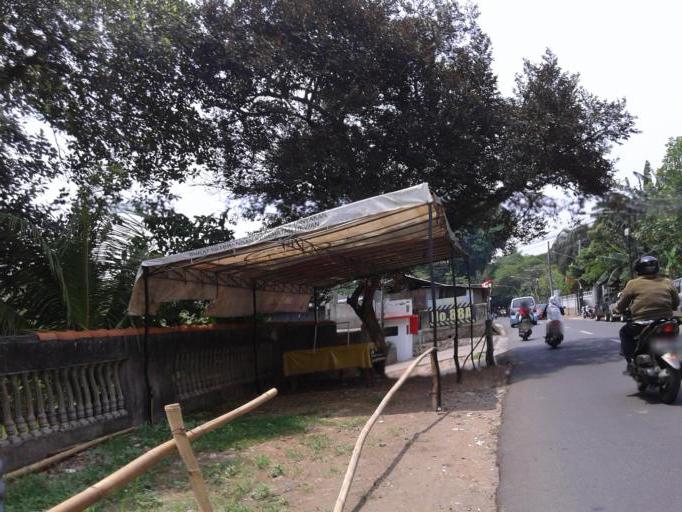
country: ID
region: West Java
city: Pamulang
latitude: -6.3211
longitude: 106.8142
